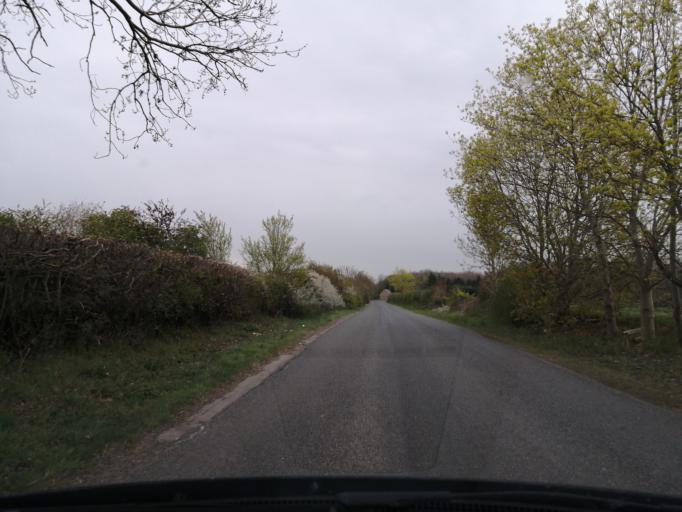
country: GB
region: England
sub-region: Peterborough
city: Wittering
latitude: 52.5943
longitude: -0.4592
